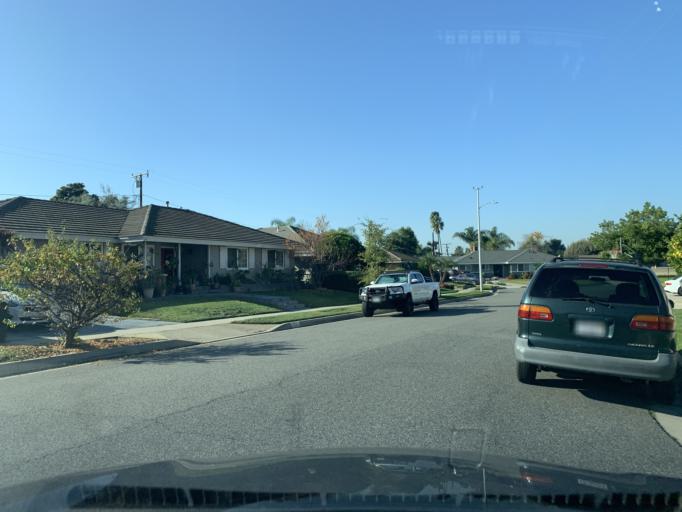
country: US
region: California
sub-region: Los Angeles County
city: Covina
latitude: 34.0776
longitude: -117.8779
